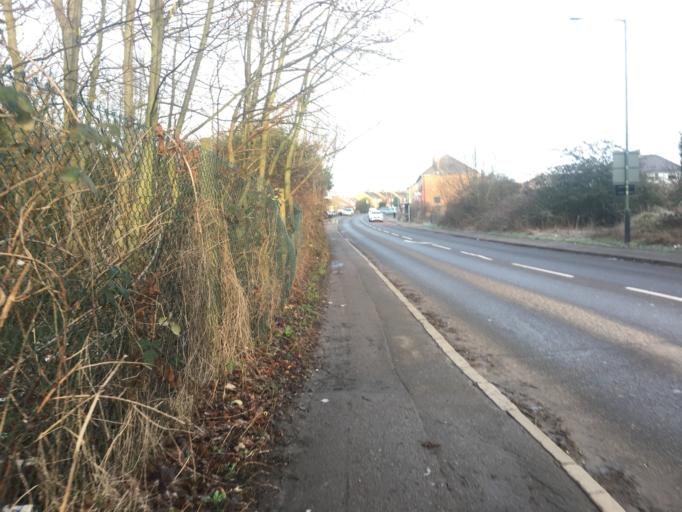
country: GB
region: England
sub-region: Warwickshire
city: Rugby
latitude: 52.3836
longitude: -1.2481
